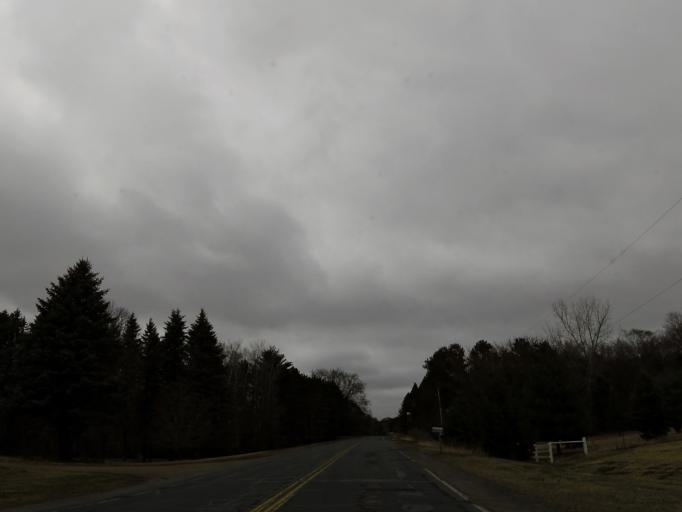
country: US
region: Minnesota
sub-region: Washington County
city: Oak Park Heights
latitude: 45.0133
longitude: -92.8292
